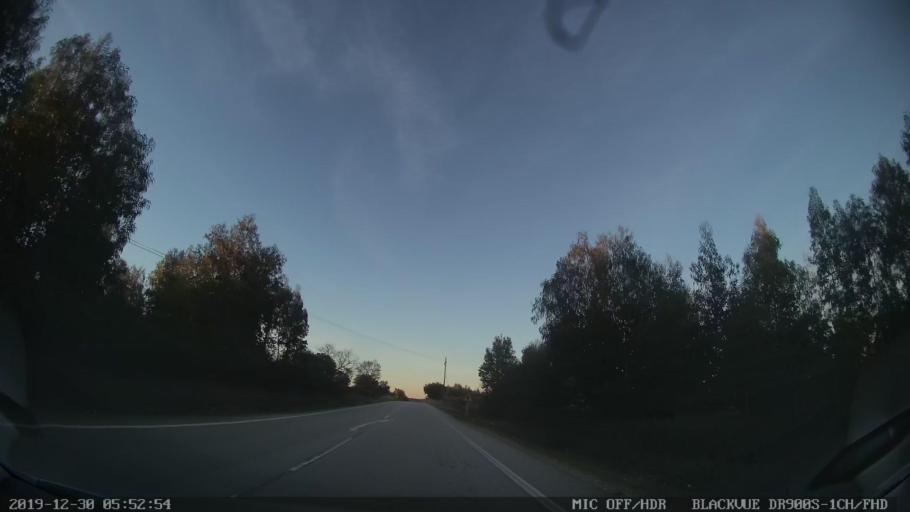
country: PT
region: Castelo Branco
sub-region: Idanha-A-Nova
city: Idanha-a-Nova
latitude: 40.0101
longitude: -7.2489
